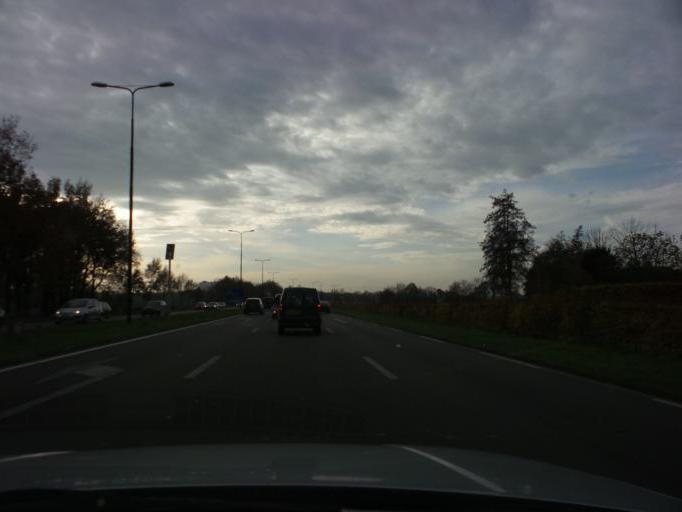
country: NL
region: Utrecht
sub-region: Gemeente Amersfoort
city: Hoogland
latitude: 52.1781
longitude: 5.3692
